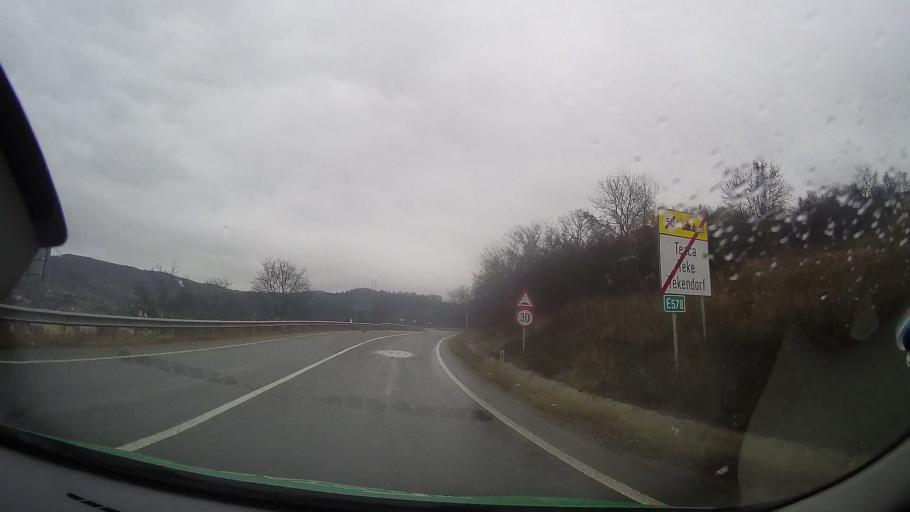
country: RO
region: Bistrita-Nasaud
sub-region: Comuna Teaca
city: Teaca
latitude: 46.9089
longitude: 24.4978
